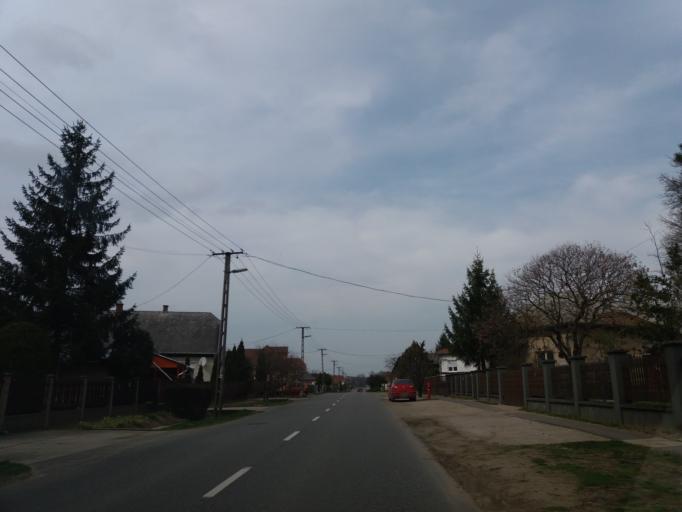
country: HU
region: Szabolcs-Szatmar-Bereg
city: Anarcs
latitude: 48.1780
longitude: 22.1004
